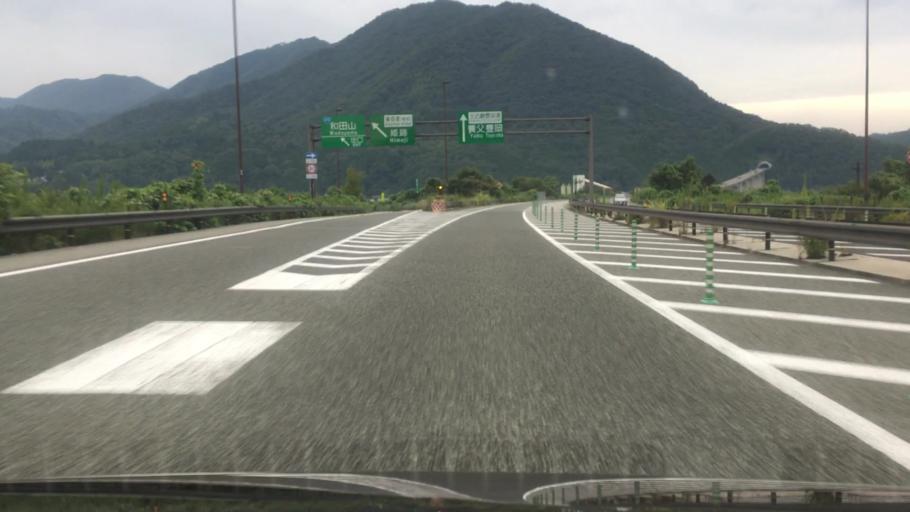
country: JP
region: Hyogo
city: Toyooka
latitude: 35.3128
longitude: 134.8497
